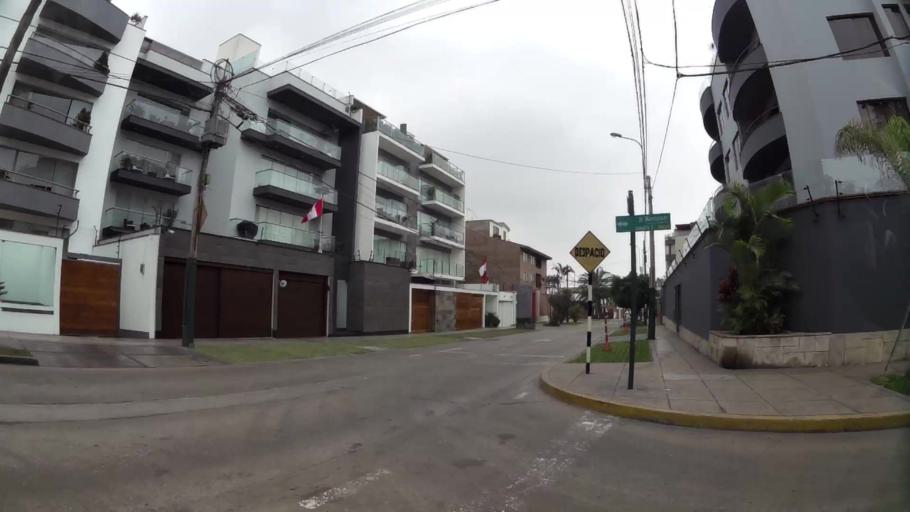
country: PE
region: Lima
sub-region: Lima
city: Surco
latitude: -12.1205
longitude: -76.9864
